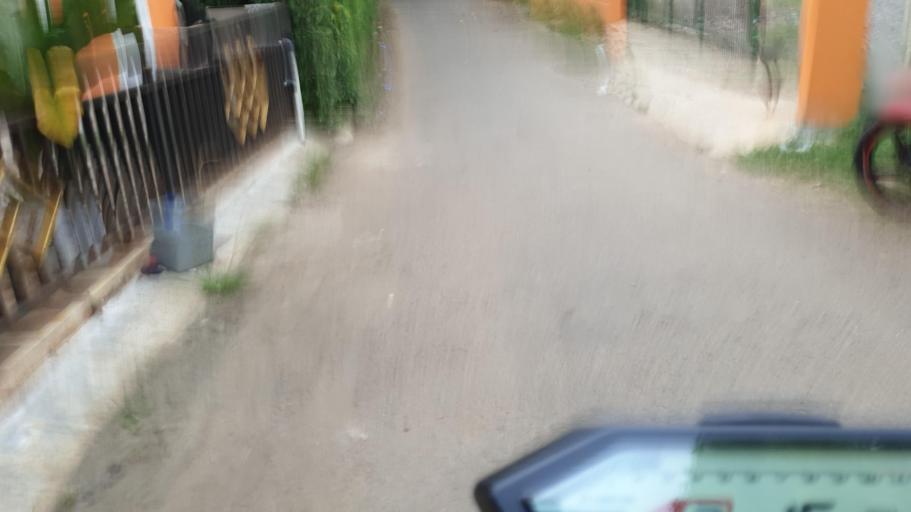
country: ID
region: West Java
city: Depok
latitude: -6.3633
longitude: 106.8389
